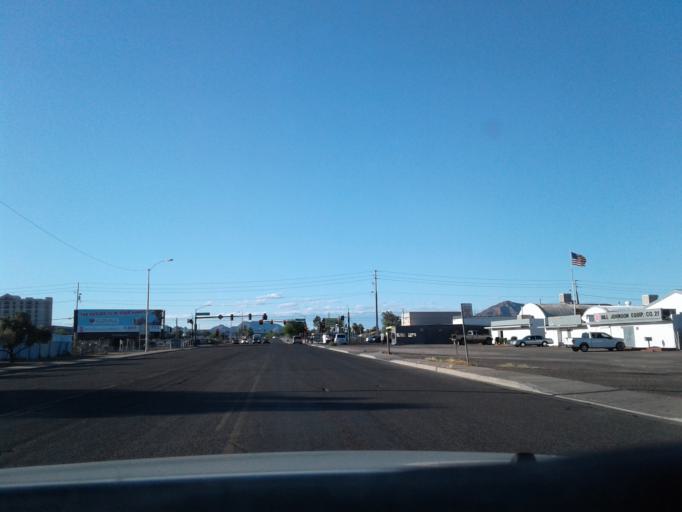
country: US
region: Arizona
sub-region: Maricopa County
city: Tempe Junction
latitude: 33.4466
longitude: -111.9954
